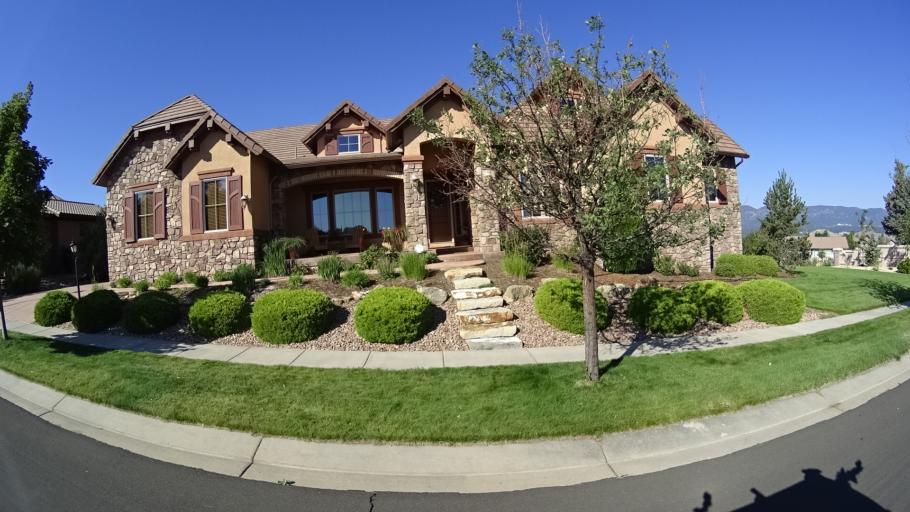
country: US
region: Colorado
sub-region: El Paso County
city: Black Forest
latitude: 38.9753
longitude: -104.7666
